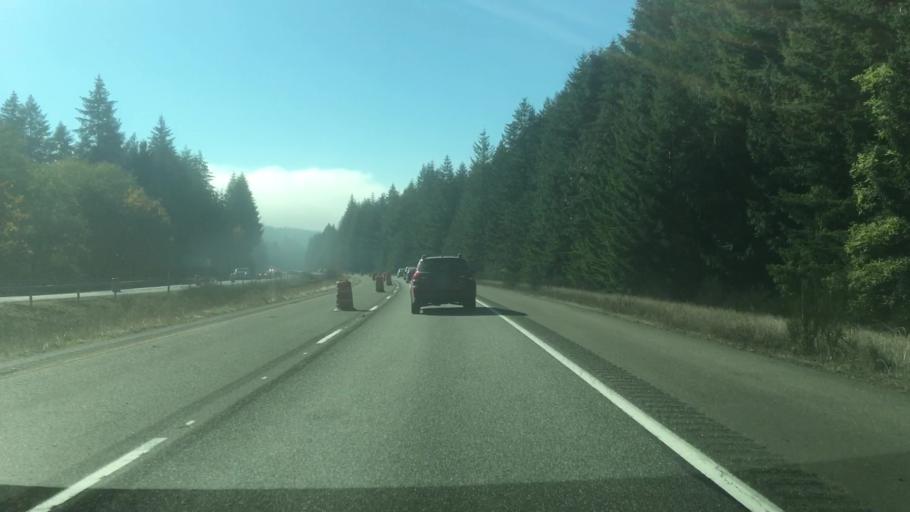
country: US
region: Washington
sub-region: Grays Harbor County
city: McCleary
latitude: 47.0481
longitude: -123.3089
